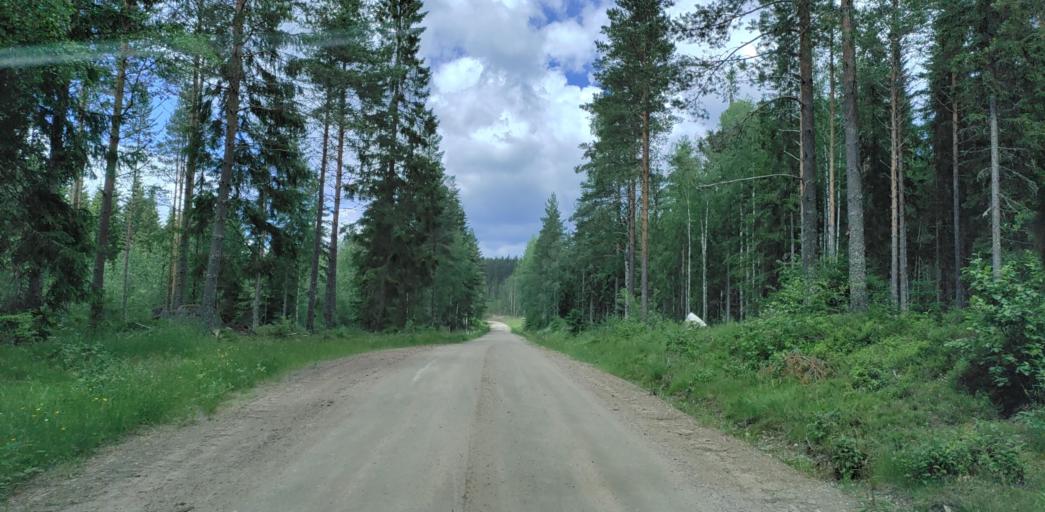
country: SE
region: Vaermland
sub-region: Hagfors Kommun
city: Ekshaerad
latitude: 60.0942
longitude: 13.4035
